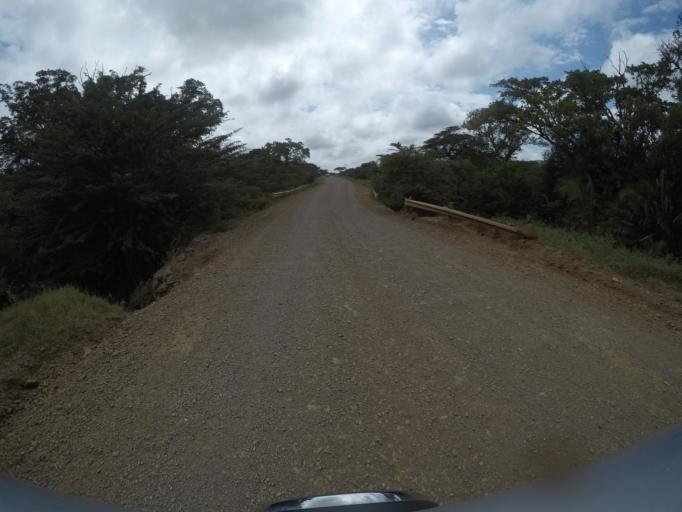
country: ZA
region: KwaZulu-Natal
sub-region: uThungulu District Municipality
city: Empangeni
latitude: -28.5892
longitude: 31.8425
